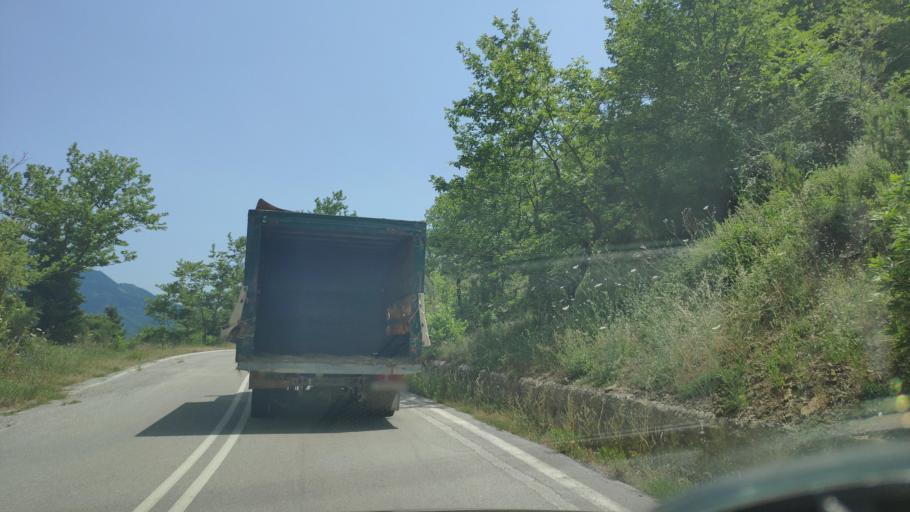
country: GR
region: Thessaly
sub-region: Nomos Kardhitsas
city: Anthiro
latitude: 39.2724
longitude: 21.3487
